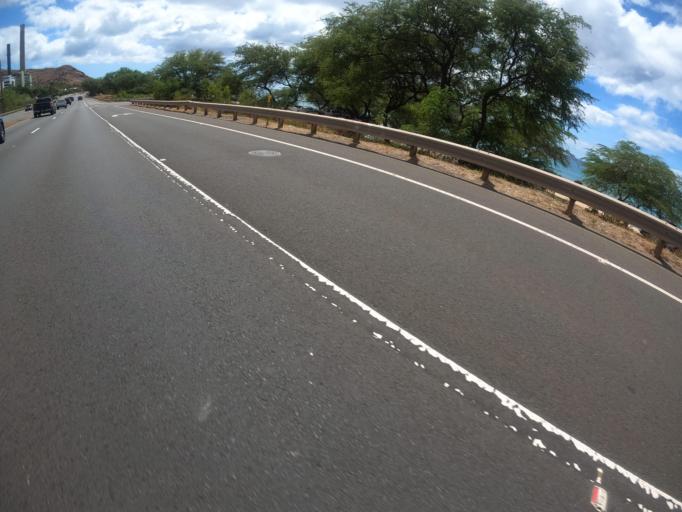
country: US
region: Hawaii
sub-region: Honolulu County
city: Nanakuli
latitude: 21.3605
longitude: -158.1317
